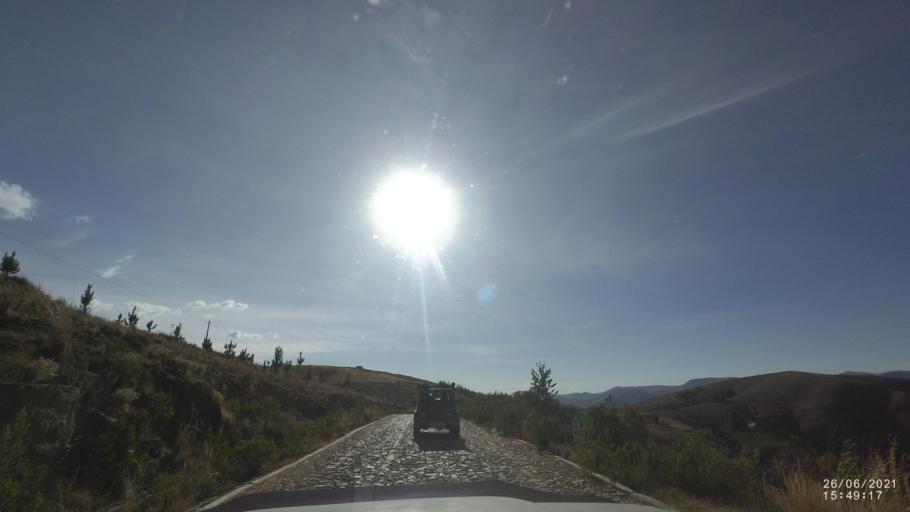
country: BO
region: Cochabamba
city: Arani
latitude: -17.8575
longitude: -65.6977
